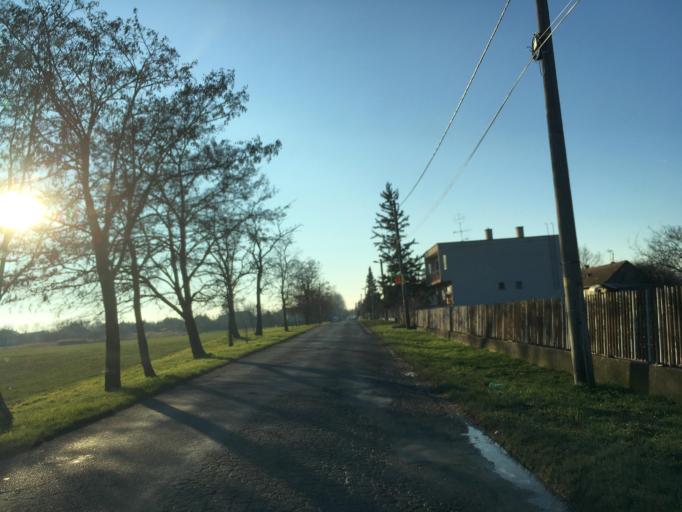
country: SK
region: Trnavsky
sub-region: Okres Dunajska Streda
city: Velky Meder
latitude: 47.8350
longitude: 17.7057
